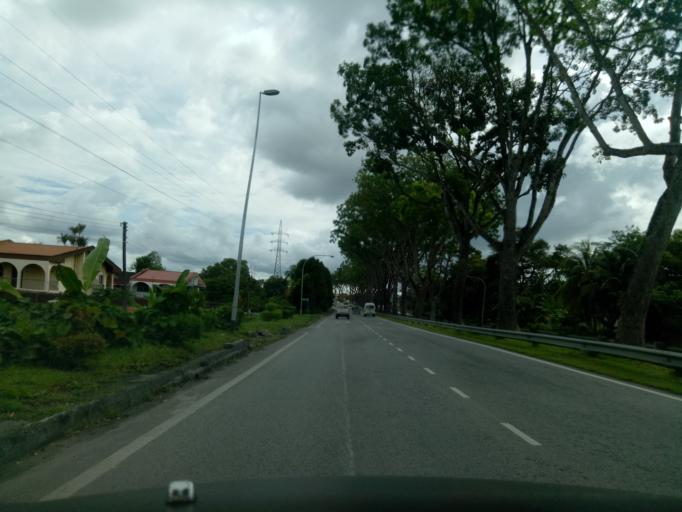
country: MY
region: Sarawak
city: Kuching
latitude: 1.5452
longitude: 110.3776
